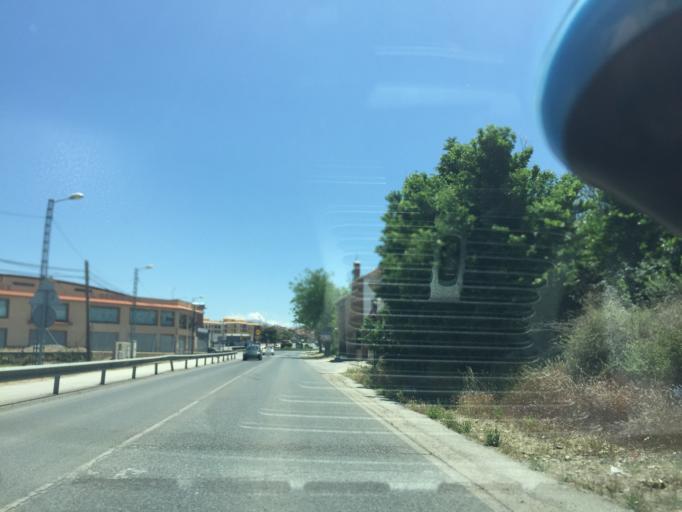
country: ES
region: Andalusia
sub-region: Provincia de Granada
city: Guadix
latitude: 37.3086
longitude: -3.1463
